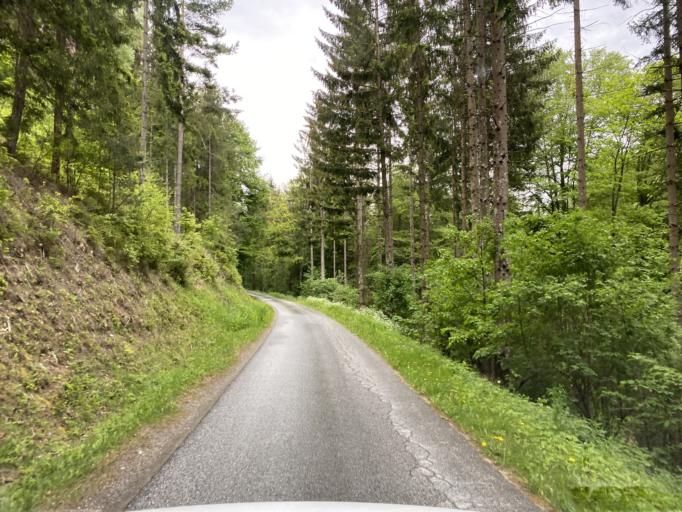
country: AT
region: Styria
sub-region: Politischer Bezirk Weiz
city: Koglhof
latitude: 47.3323
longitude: 15.6667
